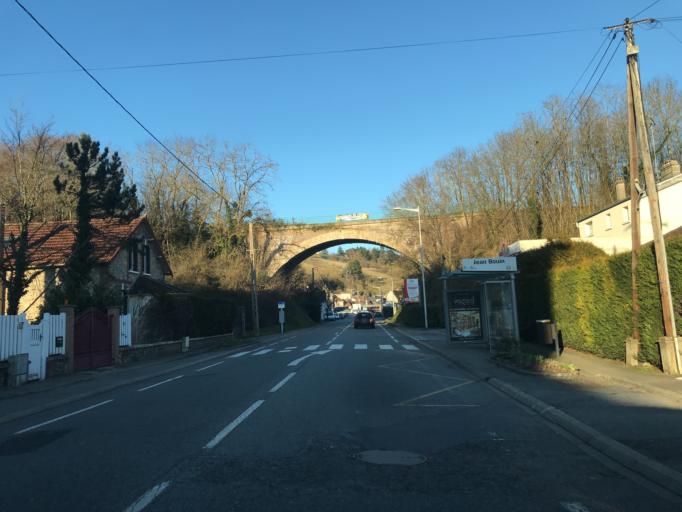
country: FR
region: Haute-Normandie
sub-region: Departement de l'Eure
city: Evreux
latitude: 49.0226
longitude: 1.1237
